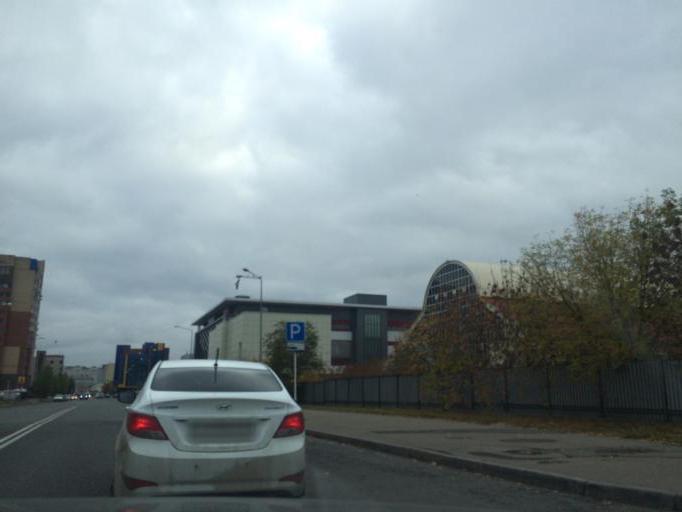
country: KZ
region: Astana Qalasy
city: Astana
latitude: 51.1500
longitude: 71.4742
